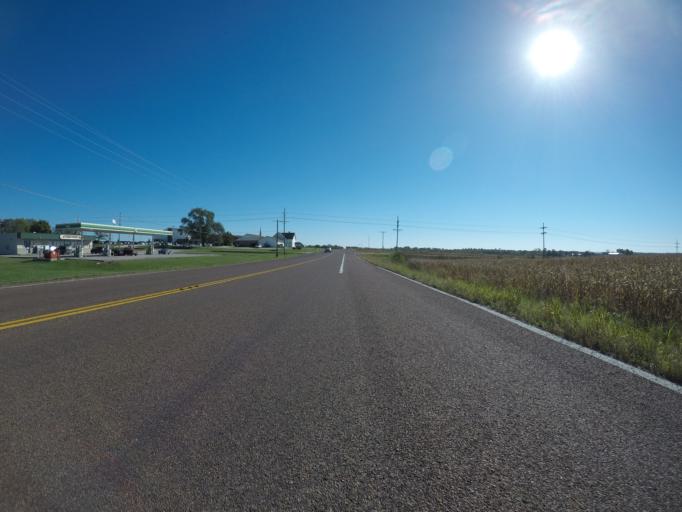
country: US
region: Kansas
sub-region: Wyandotte County
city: Bonner Springs
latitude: 39.0581
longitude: -94.9472
